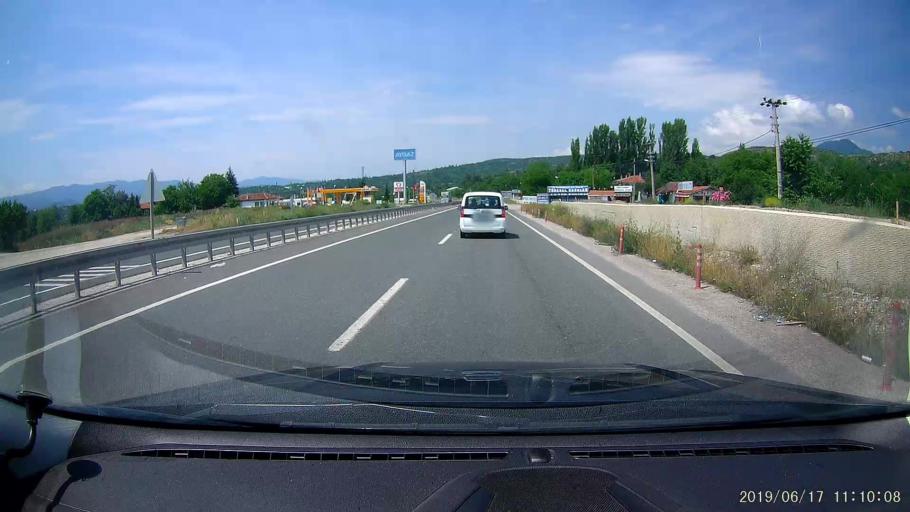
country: TR
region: Kastamonu
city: Tosya
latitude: 41.0014
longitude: 34.0291
